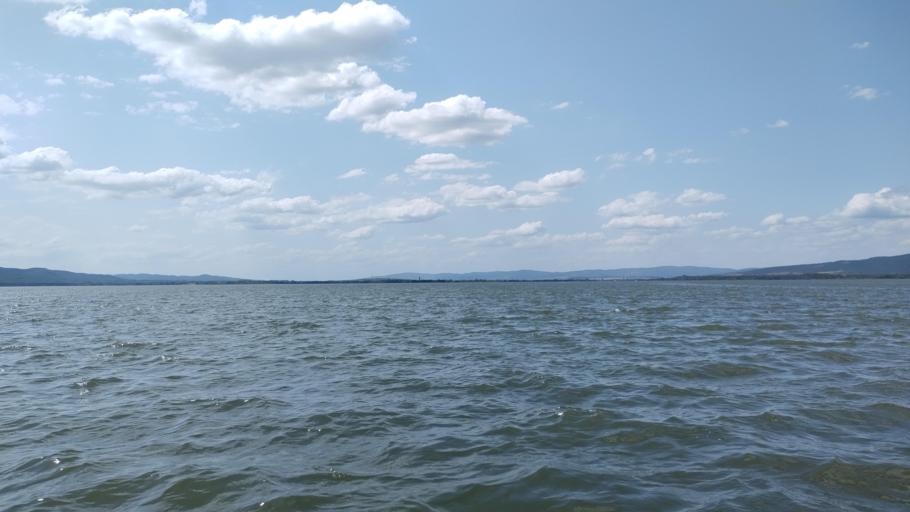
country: RO
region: Caras-Severin
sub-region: Comuna Pescari
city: Coronini
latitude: 44.6693
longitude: 21.6774
